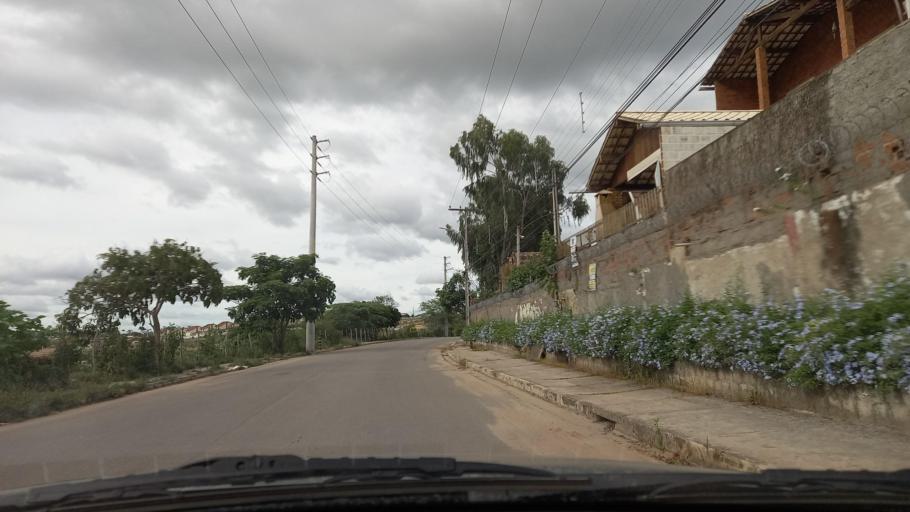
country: BR
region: Pernambuco
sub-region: Gravata
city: Gravata
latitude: -8.2045
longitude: -35.5536
